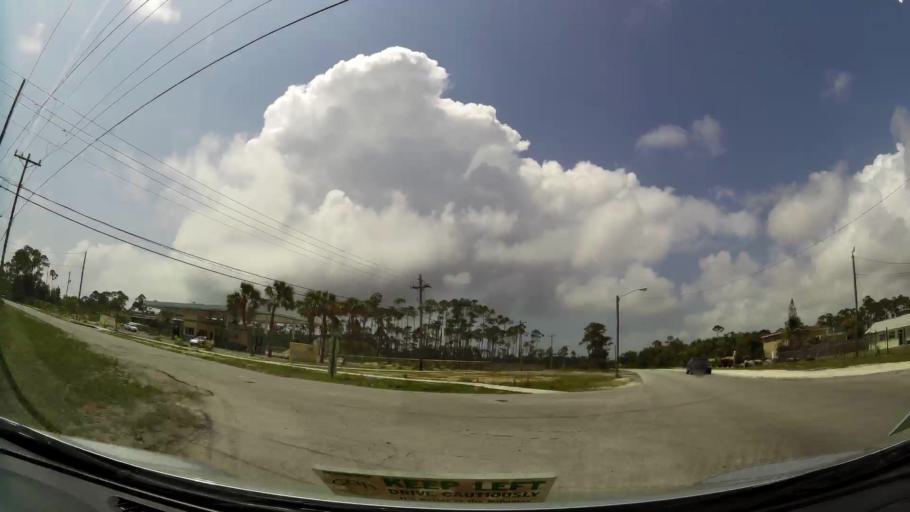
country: BS
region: Freeport
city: Lucaya
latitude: 26.5368
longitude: -78.6363
